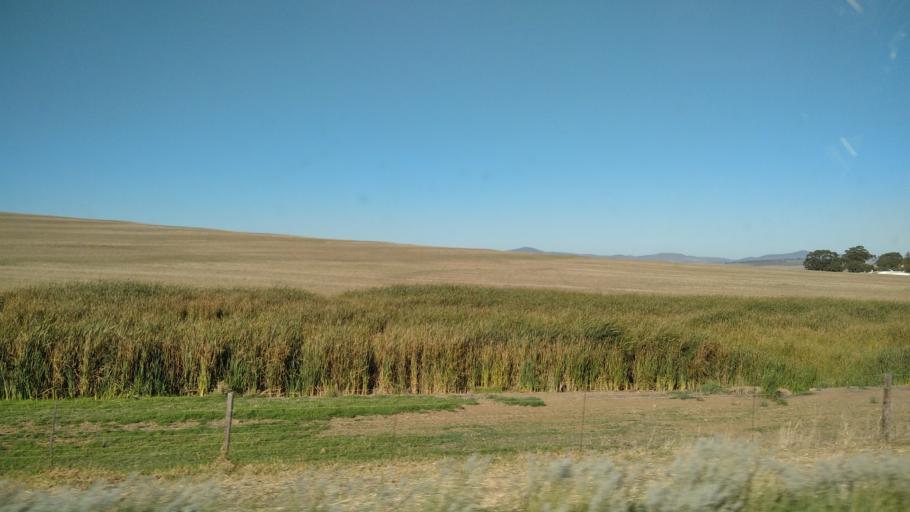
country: ZA
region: Western Cape
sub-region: West Coast District Municipality
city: Malmesbury
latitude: -33.3752
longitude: 18.6617
